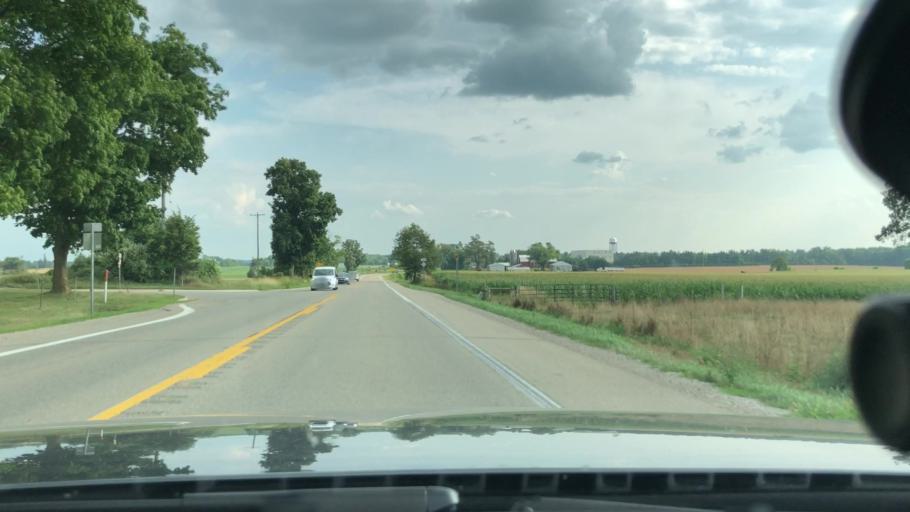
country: US
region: Michigan
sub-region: Washtenaw County
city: Chelsea
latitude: 42.2807
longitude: -84.0314
